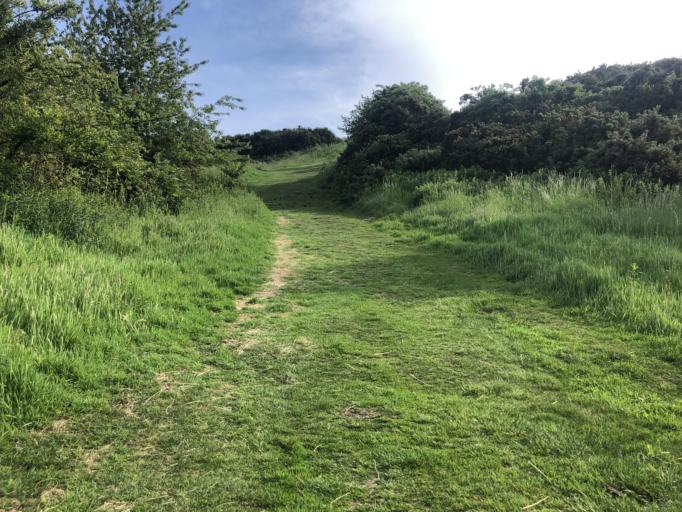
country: GB
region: Scotland
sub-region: West Lothian
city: Seafield
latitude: 55.9519
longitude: -3.1551
